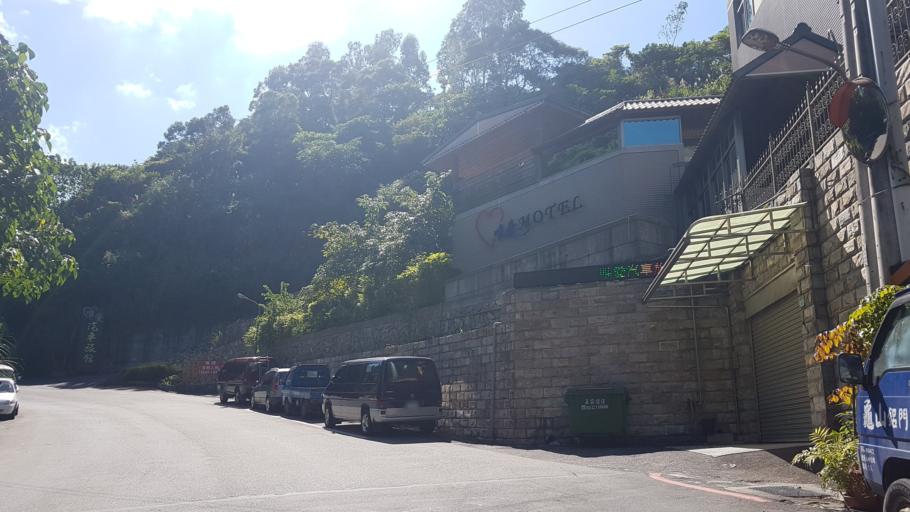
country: TW
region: Taipei
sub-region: Taipei
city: Banqiao
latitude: 24.9539
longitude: 121.5317
